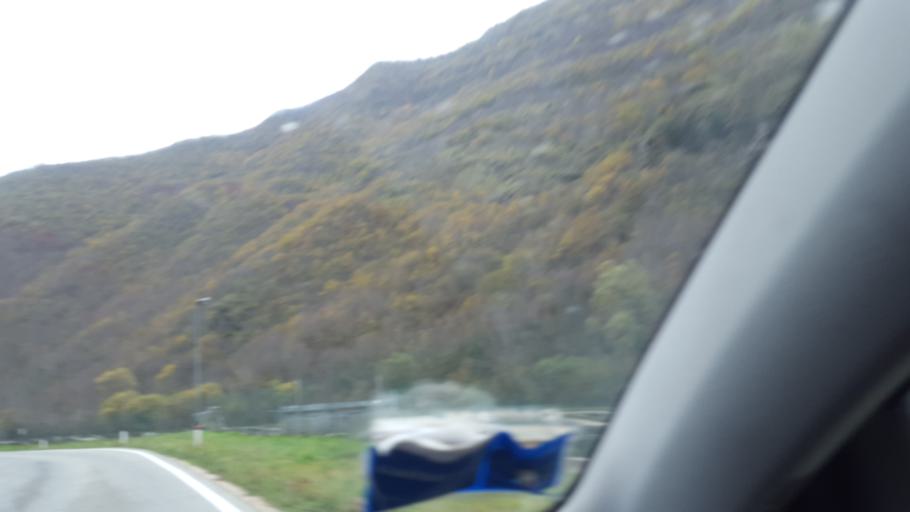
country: IT
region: The Marches
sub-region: Provincia di Macerata
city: Visso
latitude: 42.9234
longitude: 13.1052
